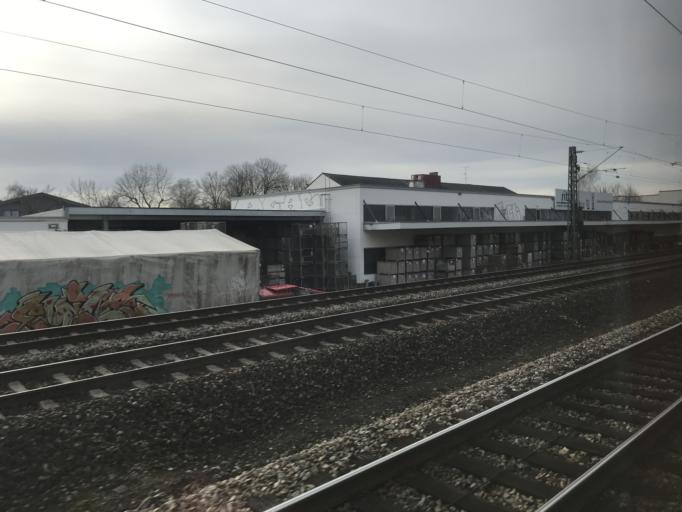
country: DE
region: Bavaria
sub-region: Upper Bavaria
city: Grobenzell
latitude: 48.1899
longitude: 11.3834
